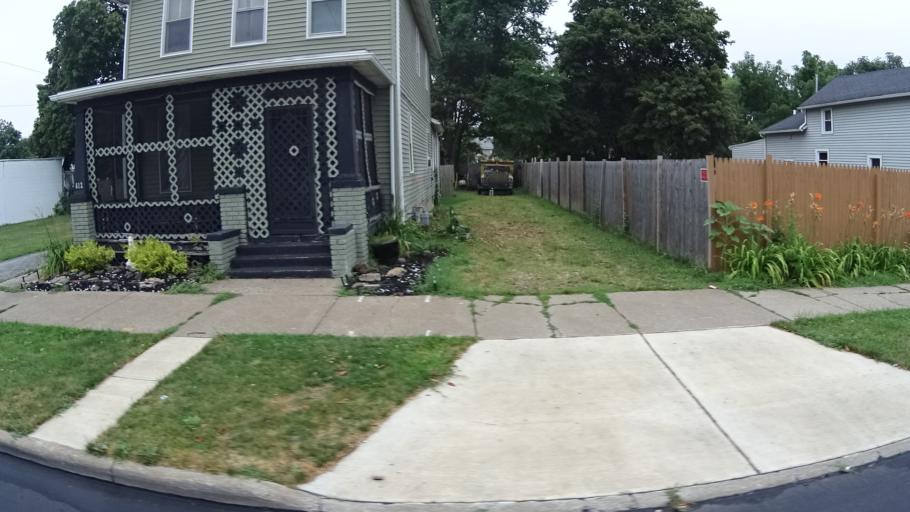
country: US
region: Ohio
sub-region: Erie County
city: Sandusky
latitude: 41.4496
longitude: -82.7040
